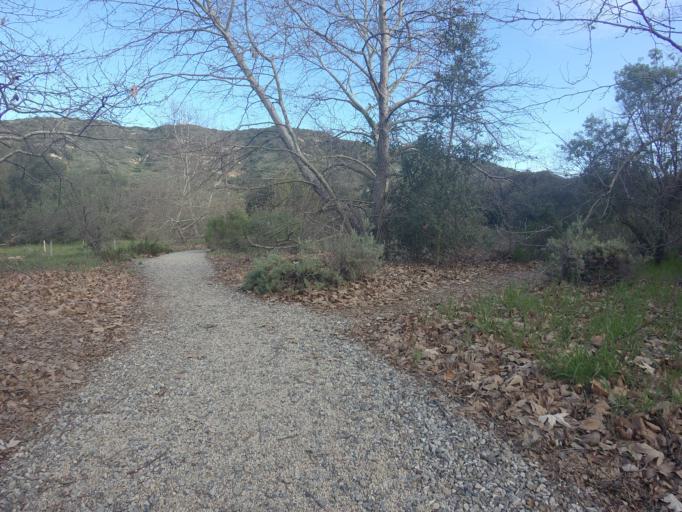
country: US
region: California
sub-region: Orange County
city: Aliso Viejo
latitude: 33.5797
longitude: -117.7631
